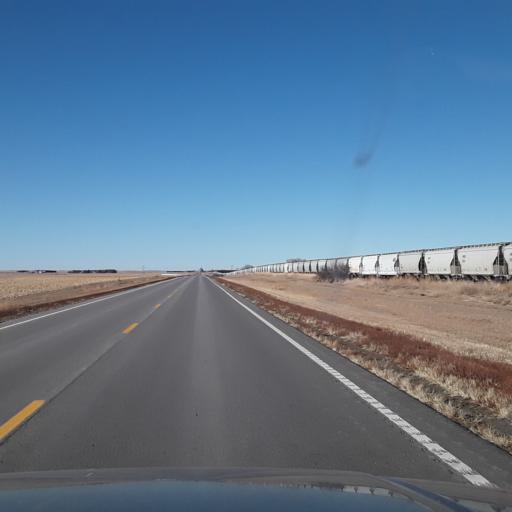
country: US
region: Nebraska
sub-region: Gosper County
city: Elwood
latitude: 40.5485
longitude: -99.6857
